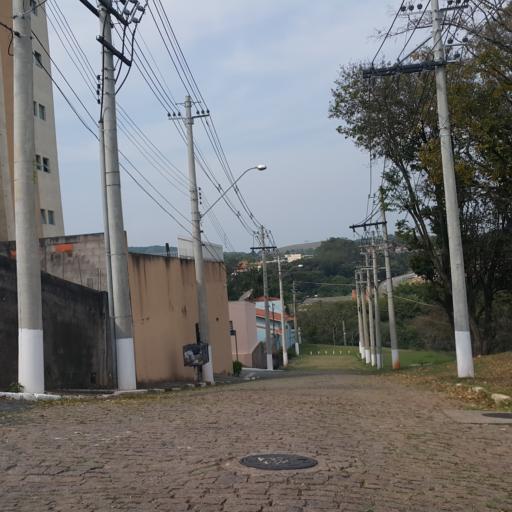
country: BR
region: Sao Paulo
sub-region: Louveira
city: Louveira
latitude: -23.0895
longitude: -46.9510
